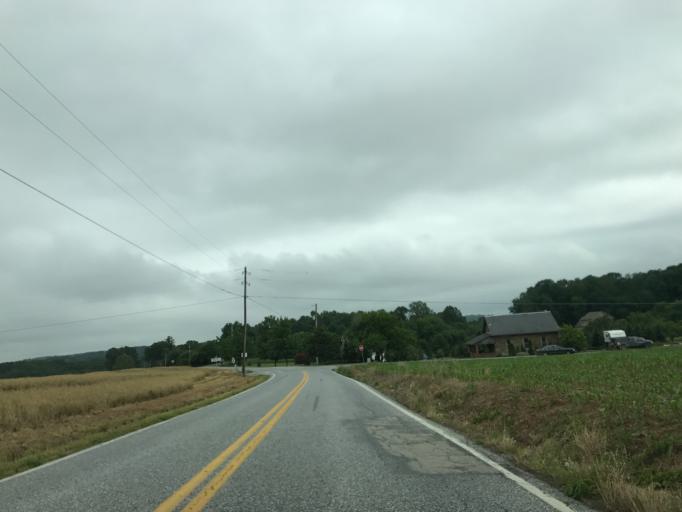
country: US
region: Pennsylvania
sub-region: York County
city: Susquehanna Trails
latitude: 39.7529
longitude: -76.4596
